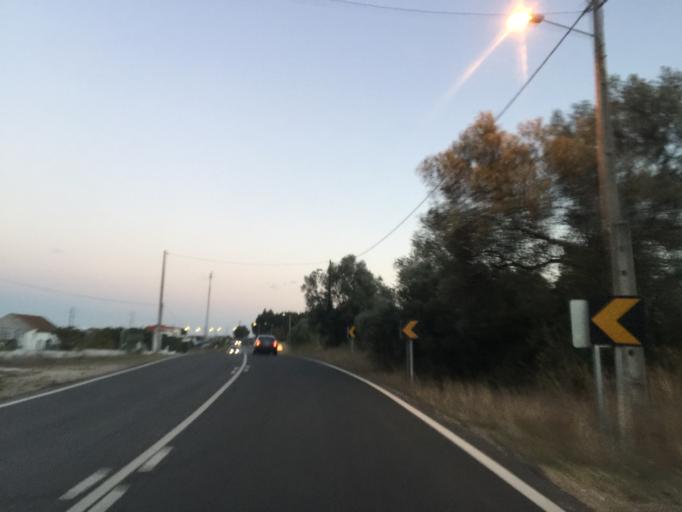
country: PT
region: Lisbon
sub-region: Alenquer
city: Alenquer
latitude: 39.1303
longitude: -8.9950
